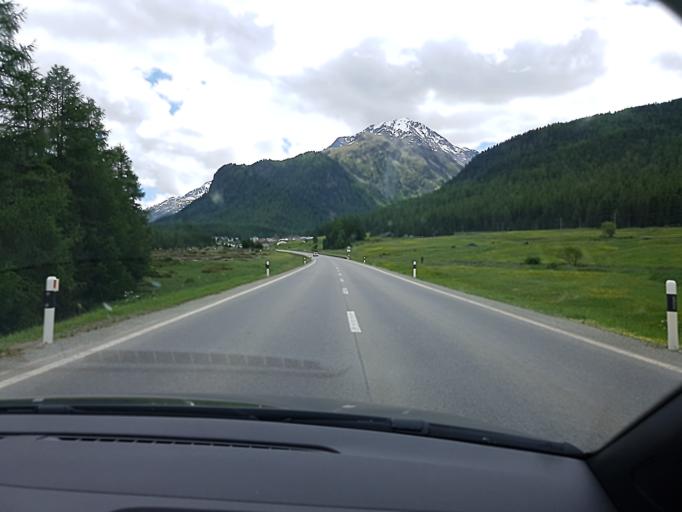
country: CH
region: Grisons
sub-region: Maloja District
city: Pontresina
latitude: 46.5012
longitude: 9.8886
